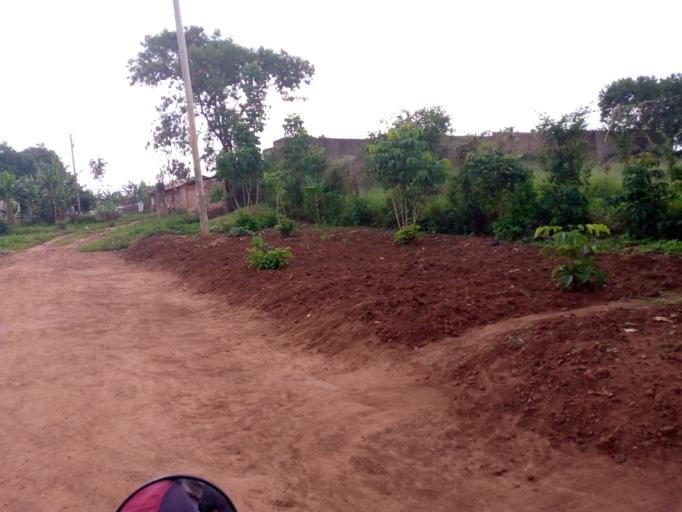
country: UG
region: Eastern Region
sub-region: Mbale District
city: Mbale
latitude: 1.0766
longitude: 34.1540
